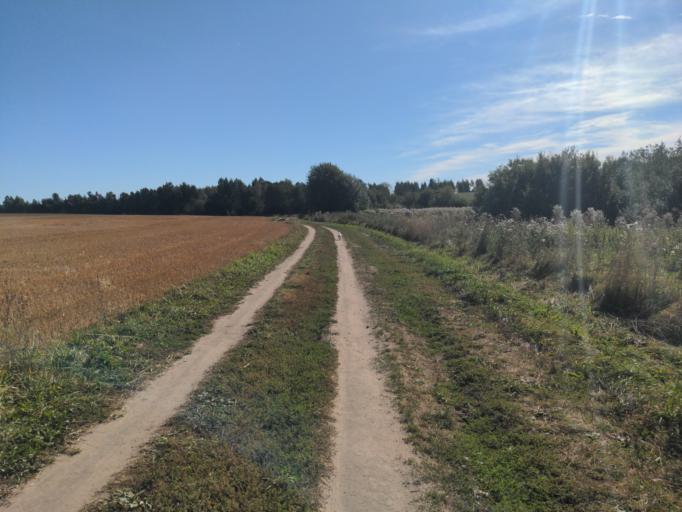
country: LT
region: Siauliu apskritis
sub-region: Siauliai
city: Siauliai
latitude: 55.9259
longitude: 23.2380
